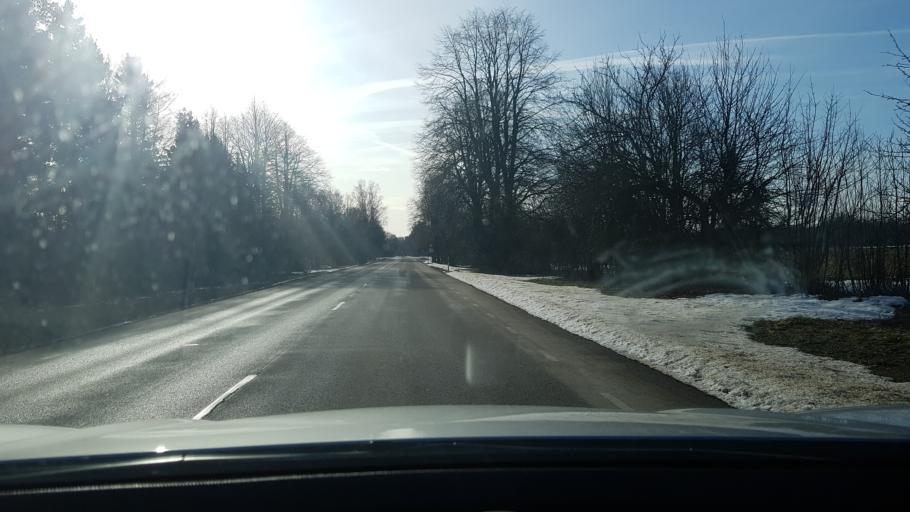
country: EE
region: Saare
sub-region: Orissaare vald
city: Orissaare
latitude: 58.5296
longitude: 23.0393
